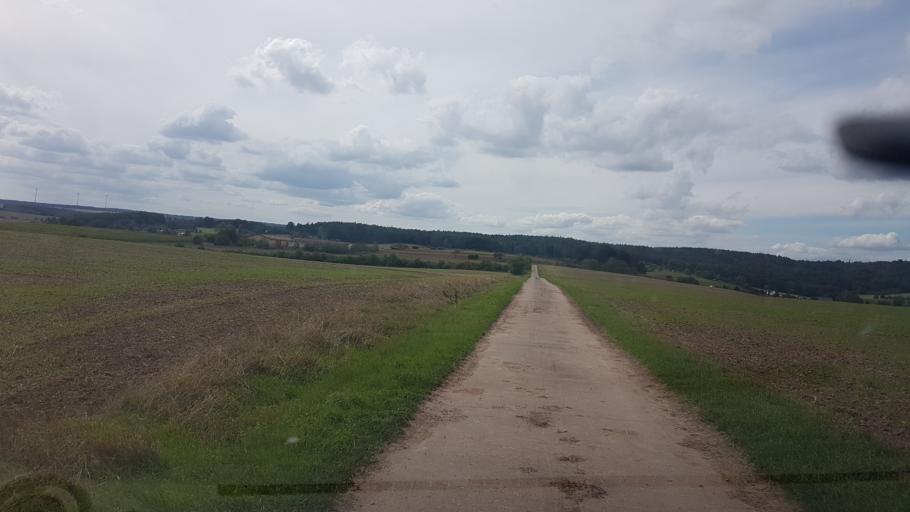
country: DE
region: Bavaria
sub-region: Upper Franconia
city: Untersiemau
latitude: 50.2071
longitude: 10.9630
